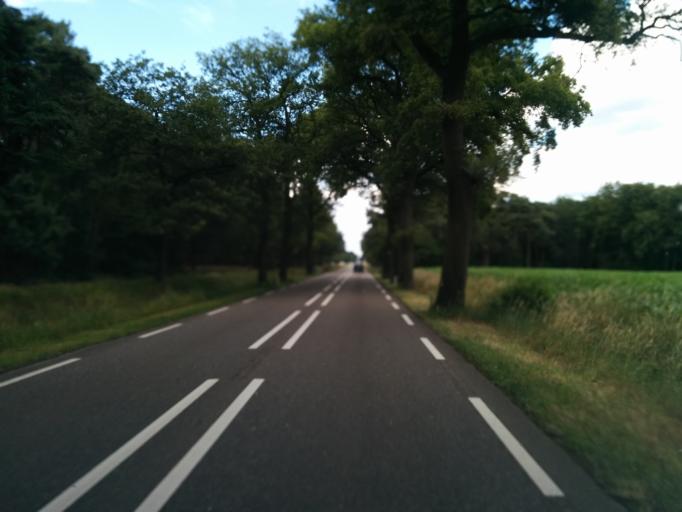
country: NL
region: North Brabant
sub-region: Gemeente Valkenswaard
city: Valkenswaard
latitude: 51.3023
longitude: 5.4194
